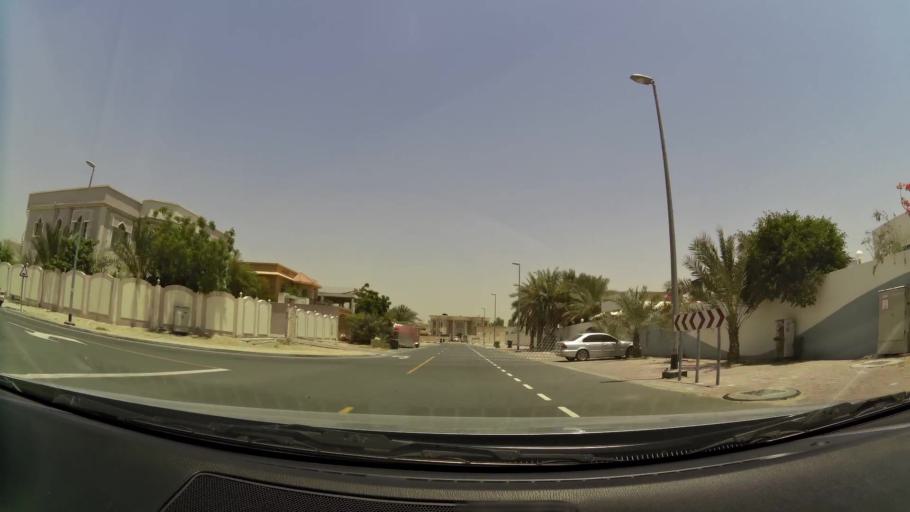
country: AE
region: Dubai
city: Dubai
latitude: 25.0988
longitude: 55.1863
